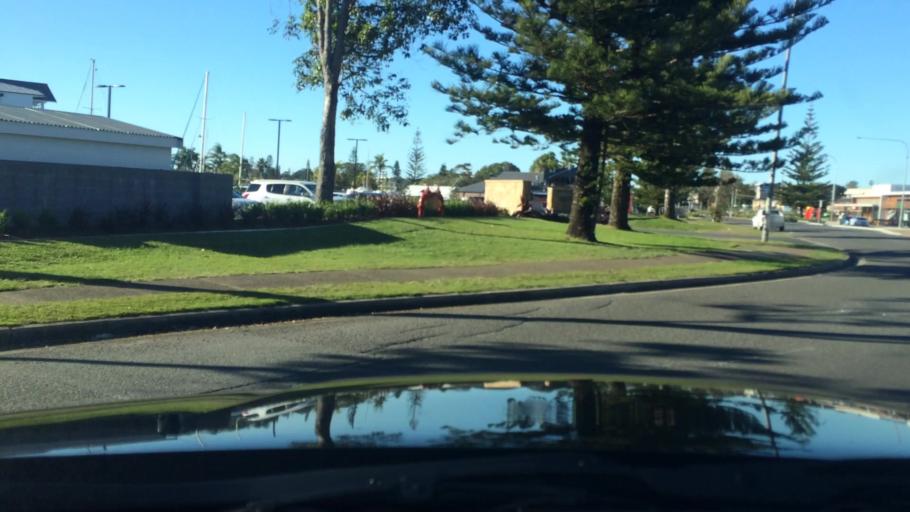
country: AU
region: New South Wales
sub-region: Port Macquarie-Hastings
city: Port Macquarie
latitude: -31.4273
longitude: 152.8972
